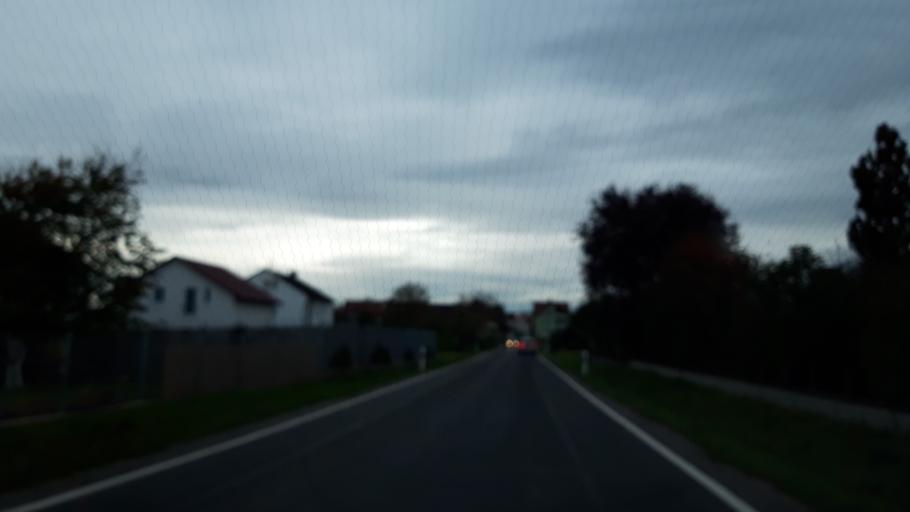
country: DE
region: Bavaria
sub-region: Regierungsbezirk Unterfranken
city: Marktheidenfeld
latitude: 49.8020
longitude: 9.5845
